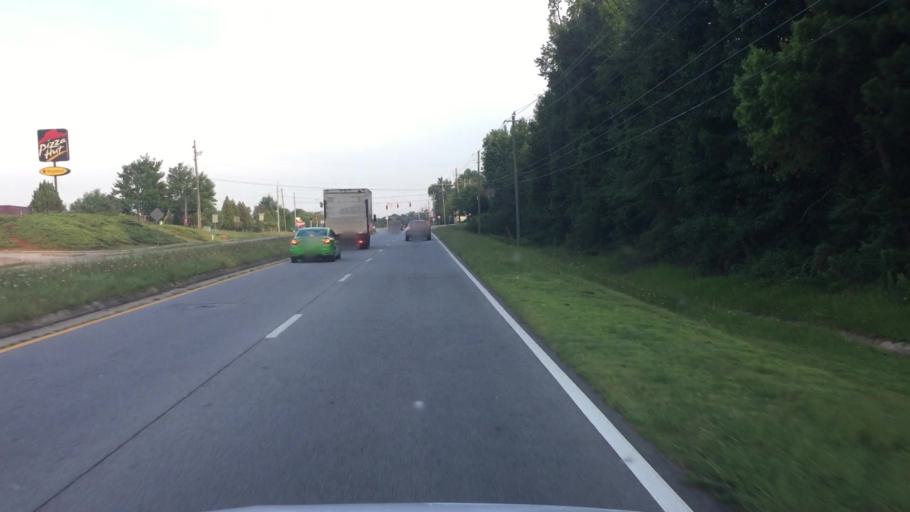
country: US
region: Georgia
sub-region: DeKalb County
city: Panthersville
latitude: 33.6800
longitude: -84.2242
